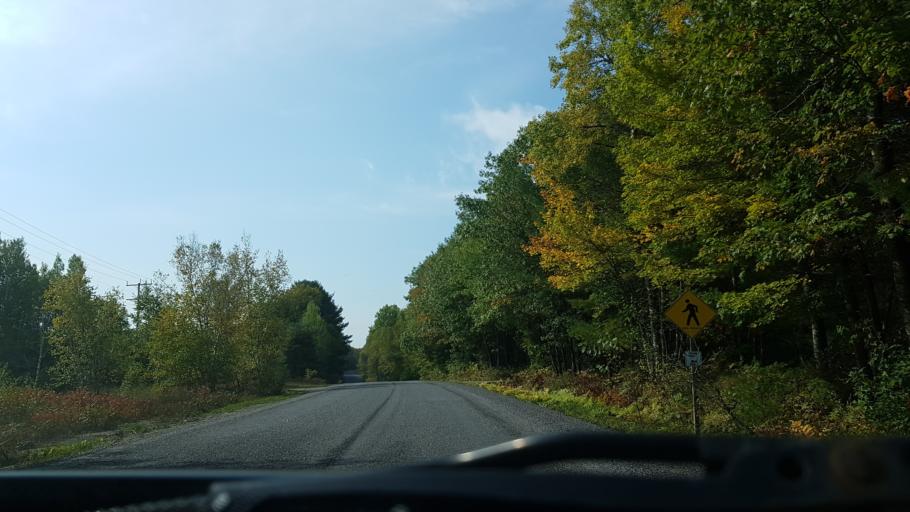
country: CA
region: Ontario
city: Gravenhurst
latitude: 44.8396
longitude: -79.2121
